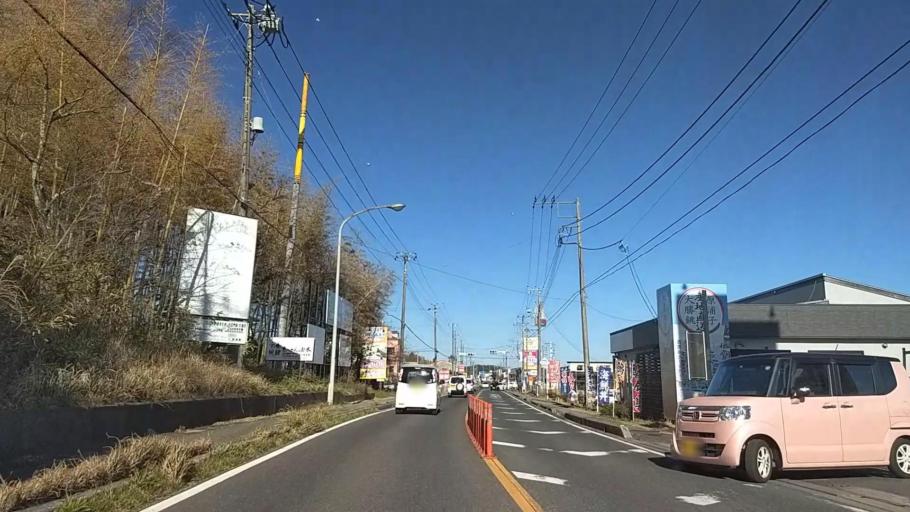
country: JP
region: Chiba
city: Ohara
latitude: 35.2882
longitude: 140.3923
